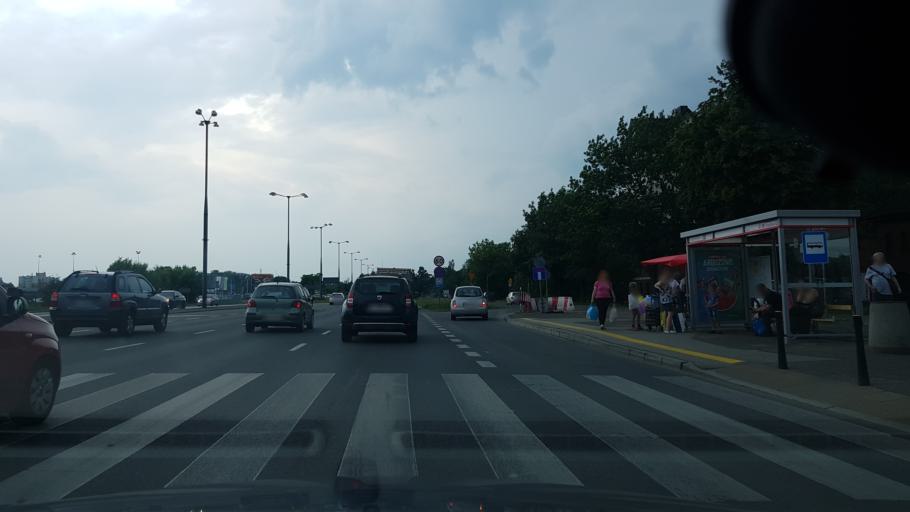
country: PL
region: Masovian Voivodeship
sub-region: Warszawa
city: Bialoleka
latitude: 52.3438
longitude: 20.9517
